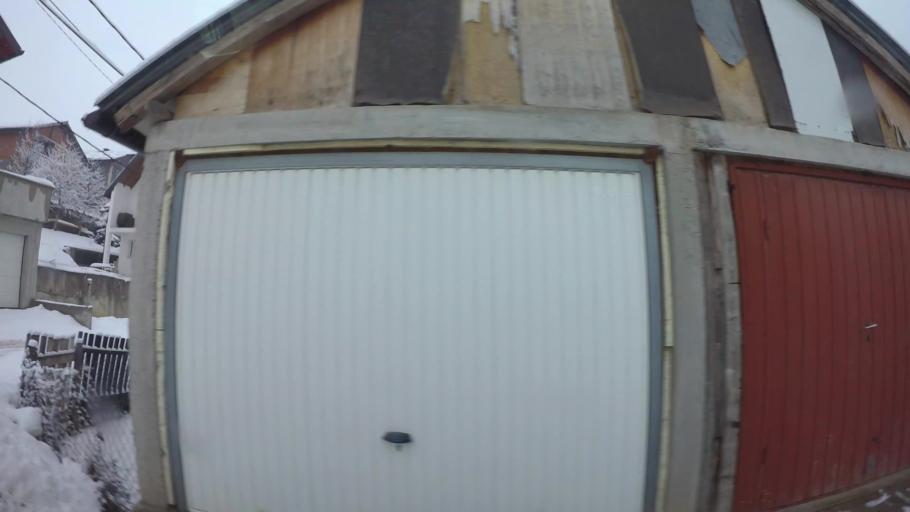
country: BA
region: Federation of Bosnia and Herzegovina
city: Vogosca
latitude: 43.8704
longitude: 18.3229
